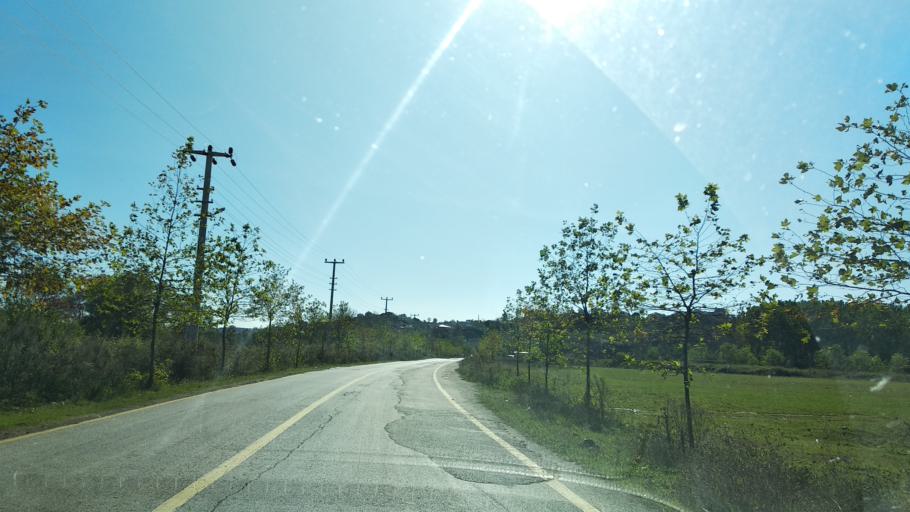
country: TR
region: Sakarya
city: Karasu
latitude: 41.1119
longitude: 30.6432
